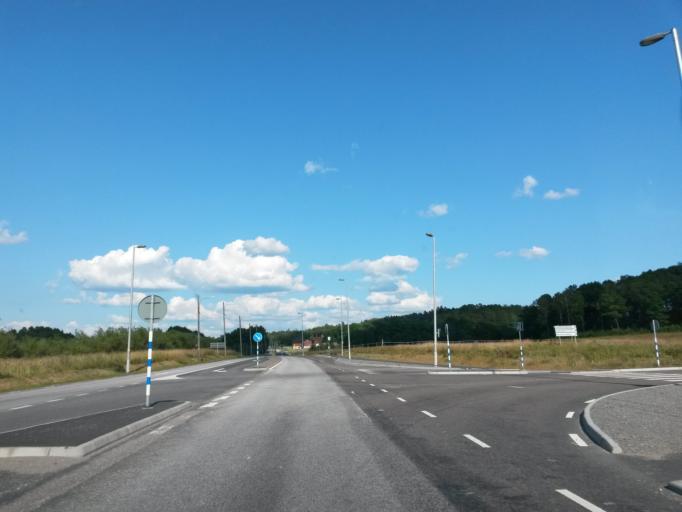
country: SE
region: Vaestra Goetaland
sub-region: Goteborg
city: Rannebergen
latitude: 57.7908
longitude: 12.1185
